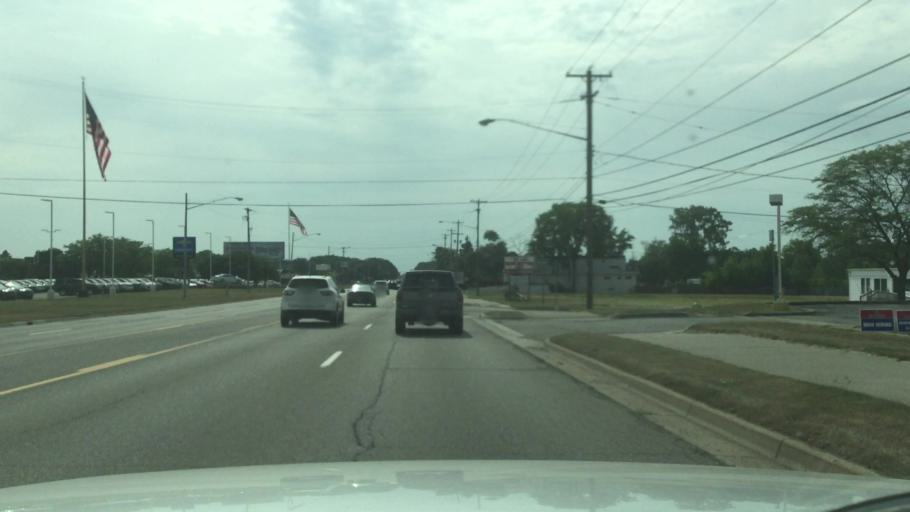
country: US
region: Michigan
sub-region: Genesee County
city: Swartz Creek
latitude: 43.0021
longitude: -83.7770
